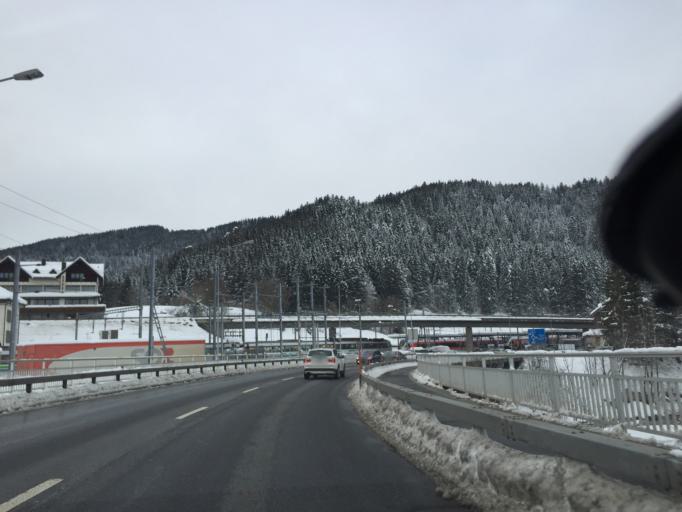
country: CH
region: Schwyz
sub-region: Bezirk Hoefe
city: Schindellegi
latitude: 47.1549
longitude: 8.7236
